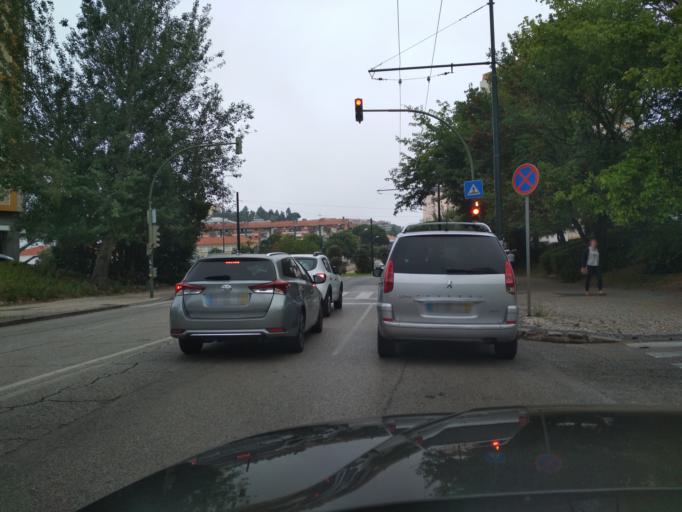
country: PT
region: Coimbra
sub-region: Coimbra
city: Coimbra
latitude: 40.2042
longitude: -8.4042
